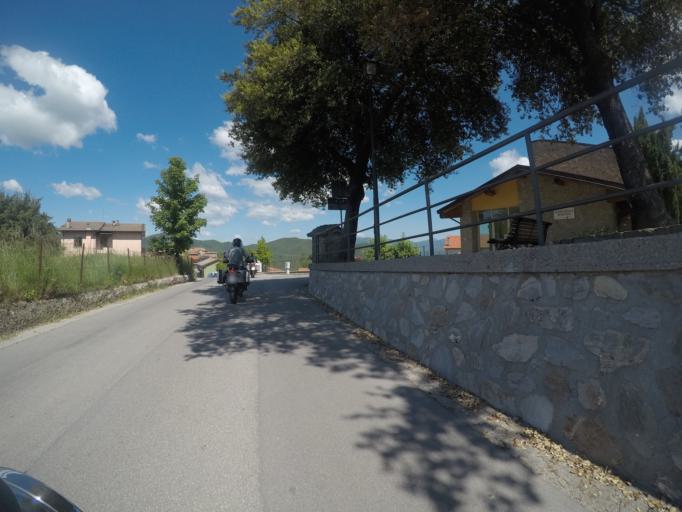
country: IT
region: Tuscany
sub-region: Provincia di Lucca
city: Careggine
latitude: 44.1197
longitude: 10.3266
